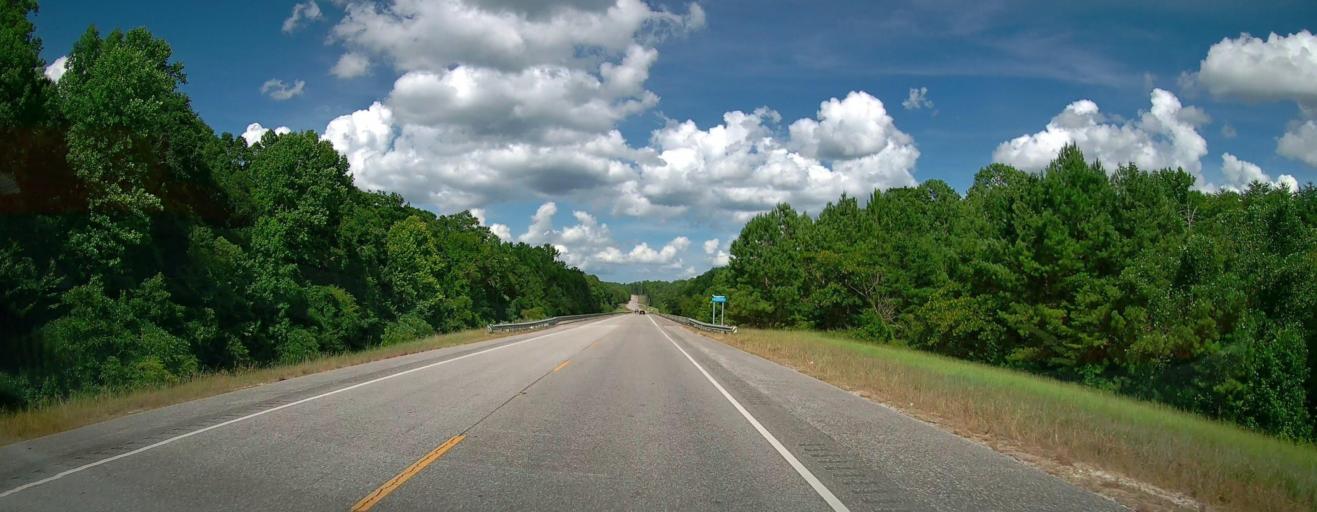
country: US
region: Alabama
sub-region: Macon County
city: Tuskegee
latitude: 32.4439
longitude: -85.6505
